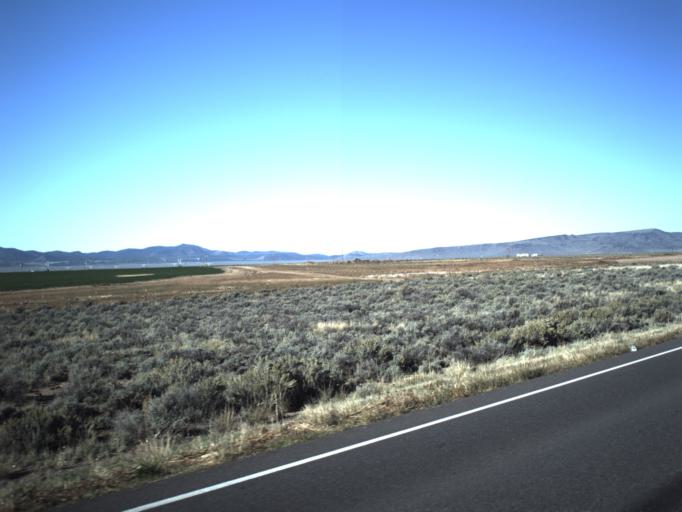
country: US
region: Utah
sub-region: Washington County
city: Enterprise
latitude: 37.7529
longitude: -113.7781
